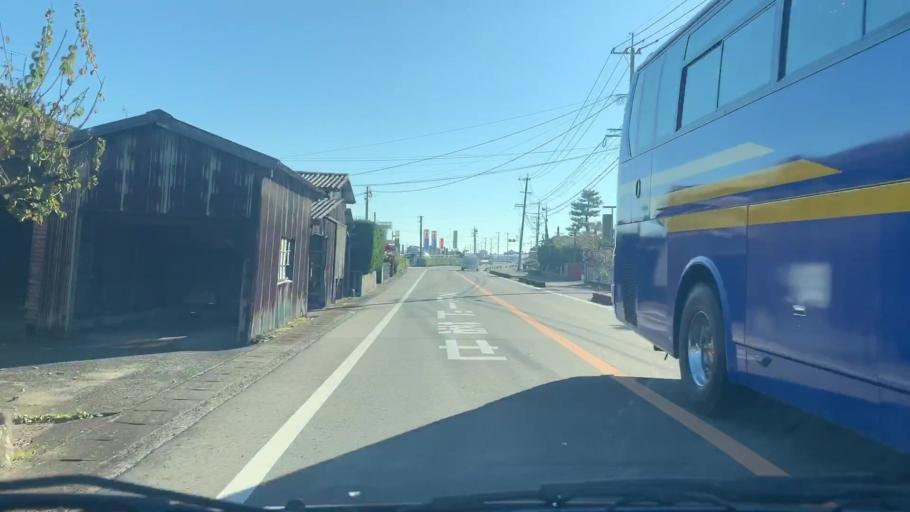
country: JP
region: Saga Prefecture
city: Kashima
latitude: 33.1941
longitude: 130.1166
